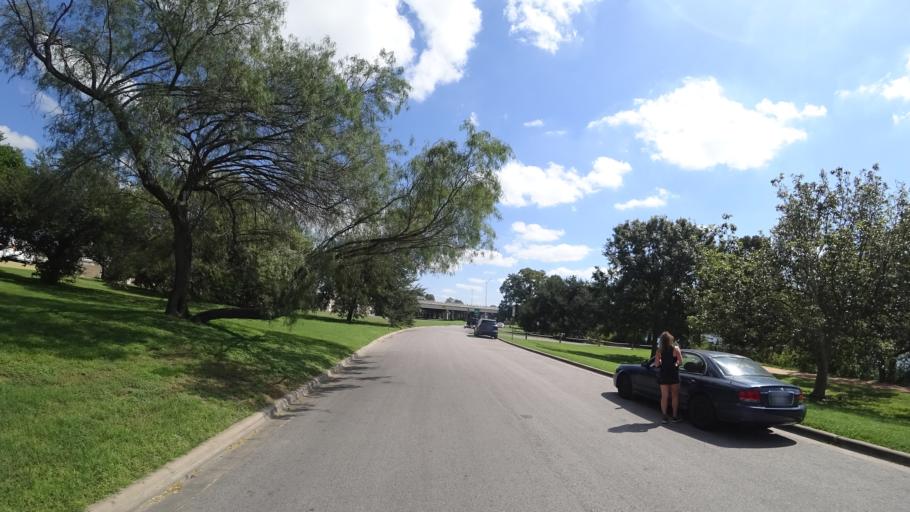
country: US
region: Texas
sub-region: Travis County
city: Austin
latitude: 30.2530
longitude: -97.7376
